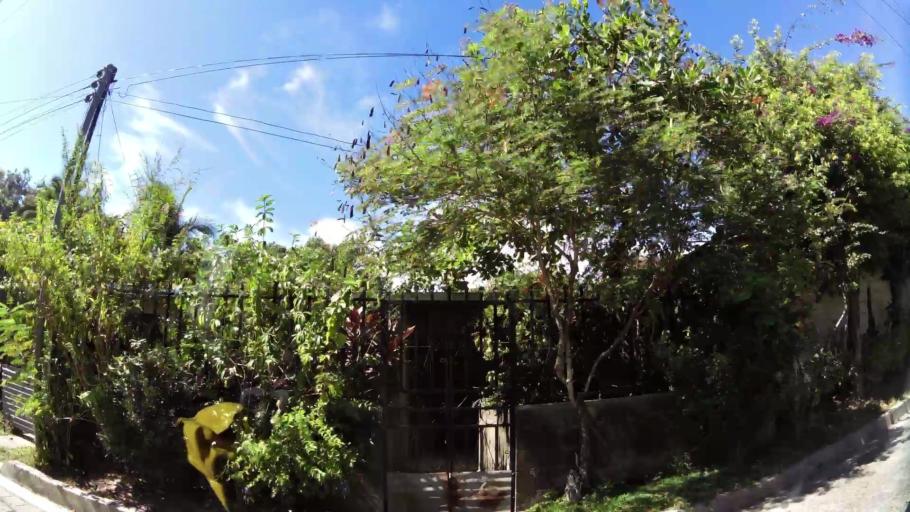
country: SV
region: San Salvador
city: Apopa
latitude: 13.8079
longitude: -89.1733
